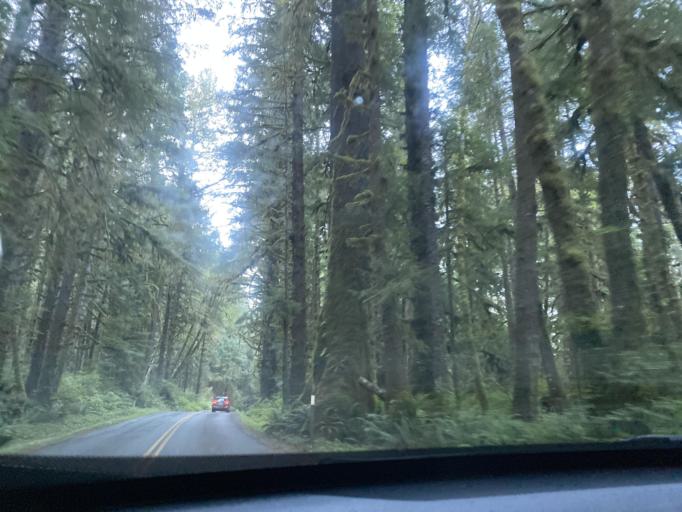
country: US
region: Washington
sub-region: Clallam County
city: Forks
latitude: 47.8142
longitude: -124.1068
